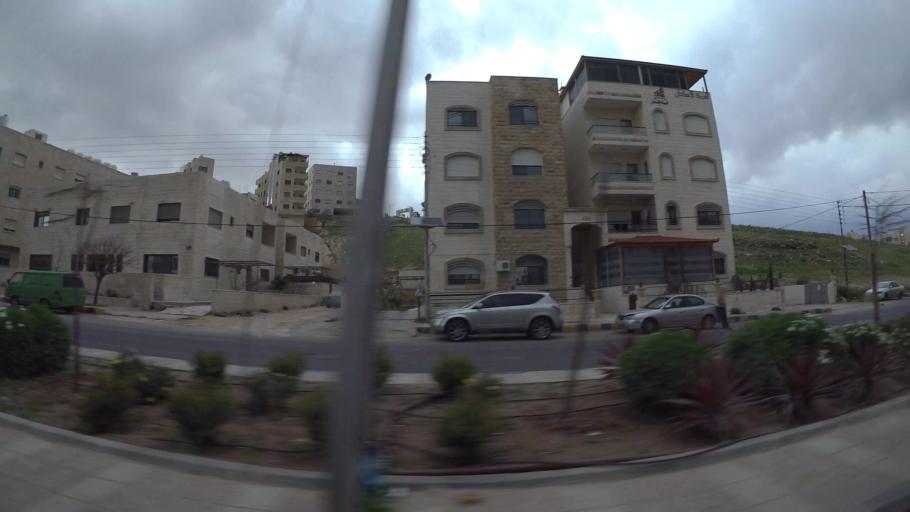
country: JO
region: Amman
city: Amman
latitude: 32.0126
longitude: 35.9527
